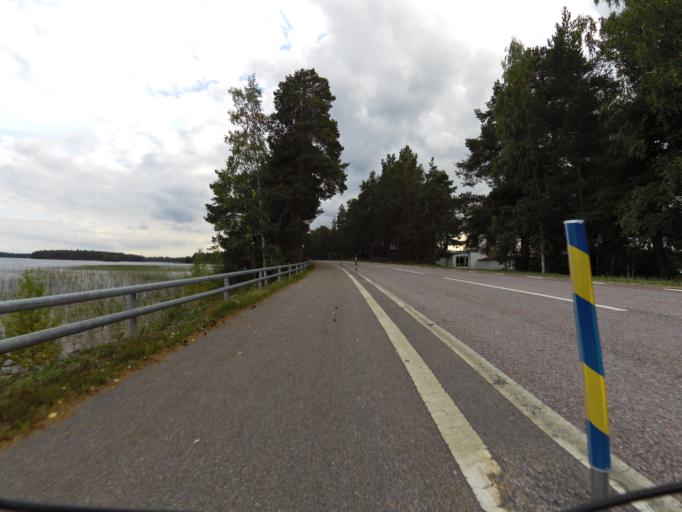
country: SE
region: Gaevleborg
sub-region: Sandvikens Kommun
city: Sandviken
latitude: 60.6969
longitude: 16.8167
